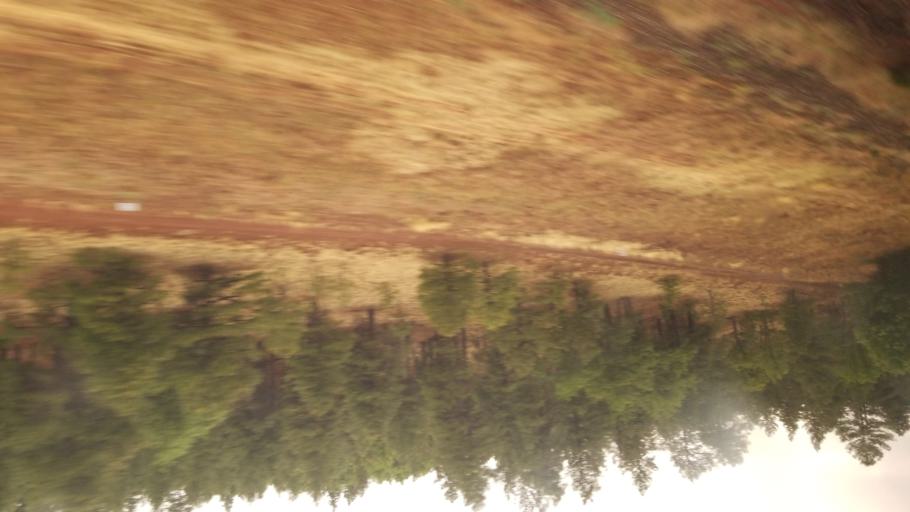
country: US
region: Arizona
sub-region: Coconino County
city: Parks
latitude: 35.2510
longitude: -111.9048
